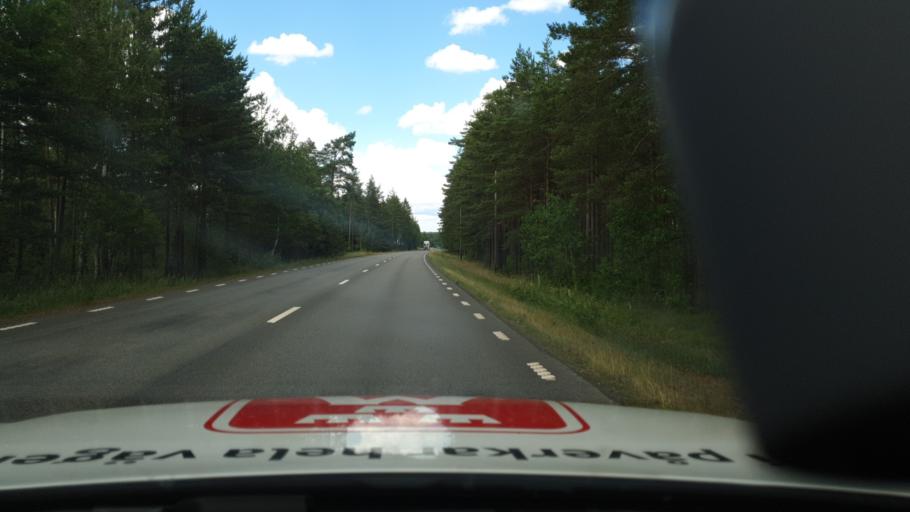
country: SE
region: Vaestra Goetaland
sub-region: Karlsborgs Kommun
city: Molltorp
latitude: 58.4774
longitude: 14.4081
